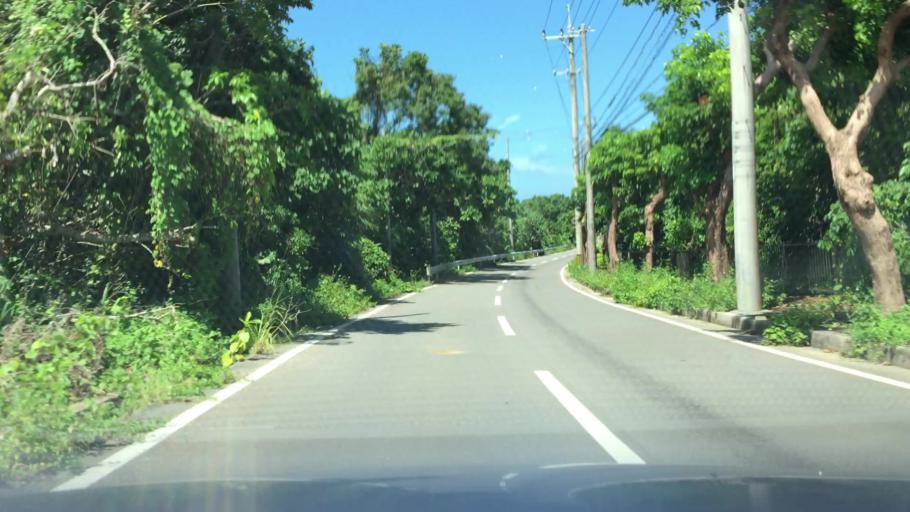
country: JP
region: Okinawa
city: Ishigaki
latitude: 24.4487
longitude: 124.1819
